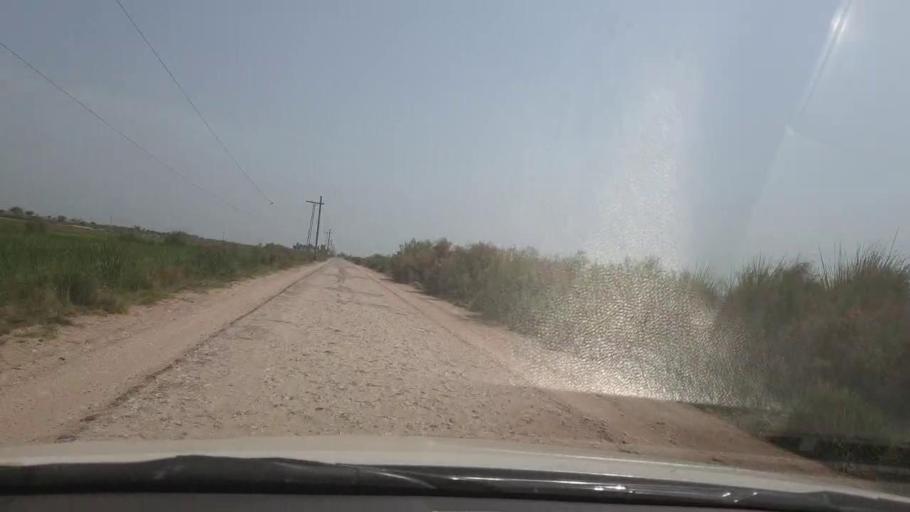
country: PK
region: Sindh
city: Garhi Yasin
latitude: 27.9647
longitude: 68.5044
